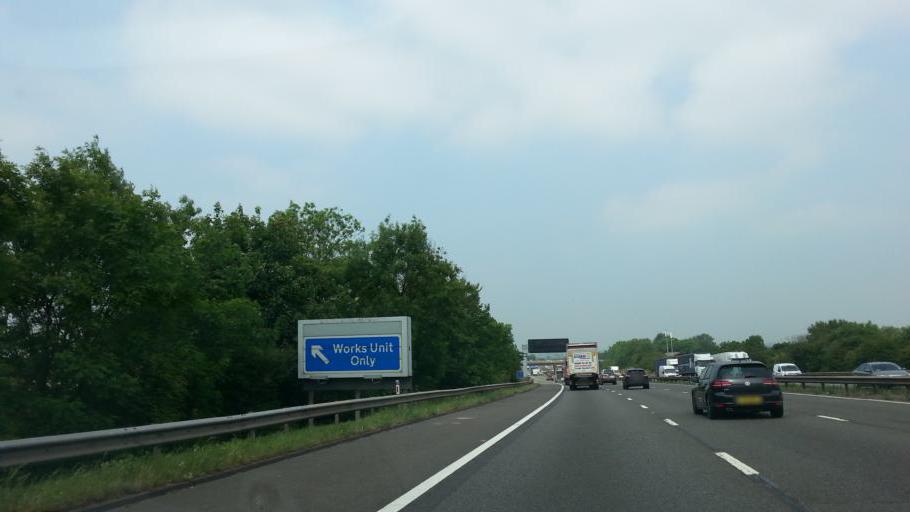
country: GB
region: England
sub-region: Staffordshire
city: Stafford
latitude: 52.8071
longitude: -2.1540
